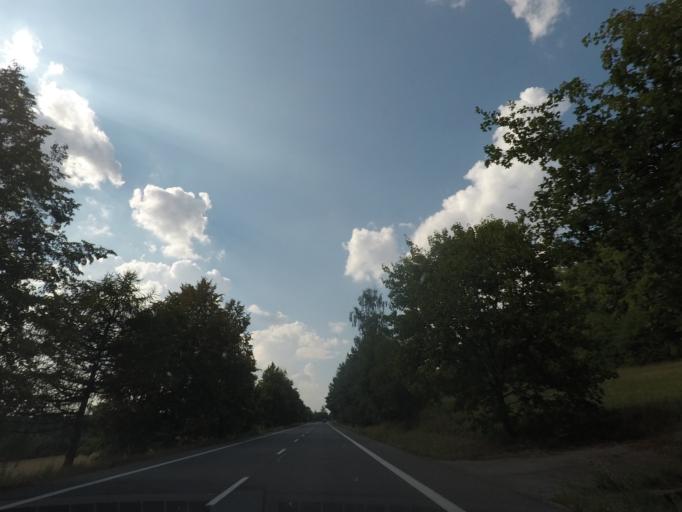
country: CZ
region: Kralovehradecky
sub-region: Okres Nachod
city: Jaromer
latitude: 50.3949
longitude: 15.9015
